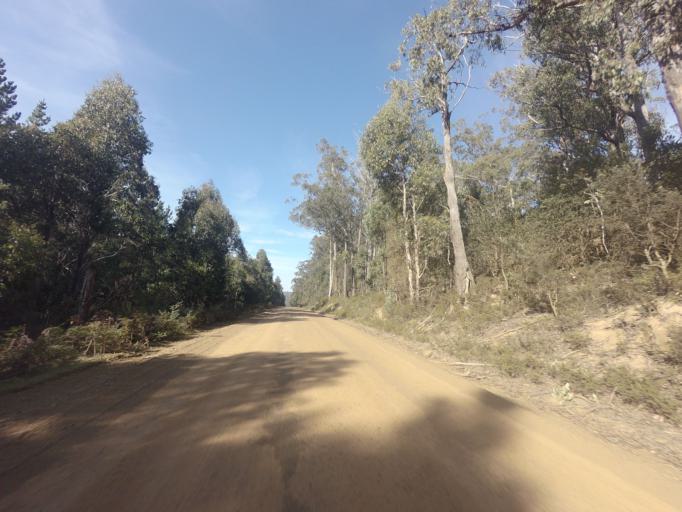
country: AU
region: Tasmania
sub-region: Sorell
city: Sorell
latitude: -42.4888
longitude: 147.5084
